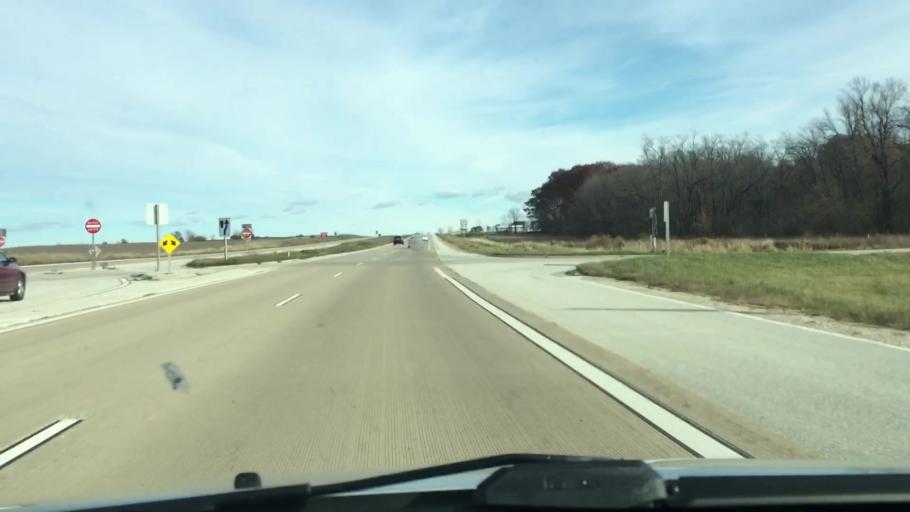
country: US
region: Wisconsin
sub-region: Kewaunee County
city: Luxemburg
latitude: 44.7169
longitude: -87.6714
